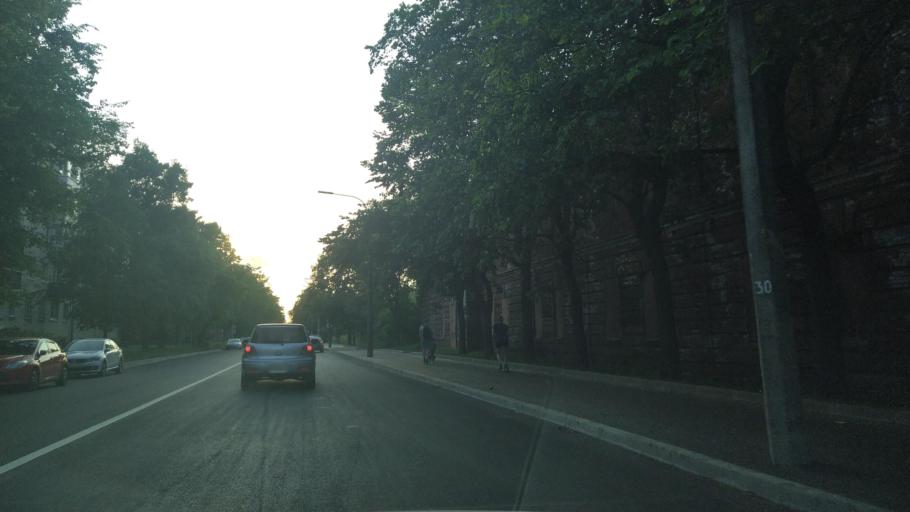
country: RU
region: St.-Petersburg
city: Kronshtadt
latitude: 59.9972
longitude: 29.7769
